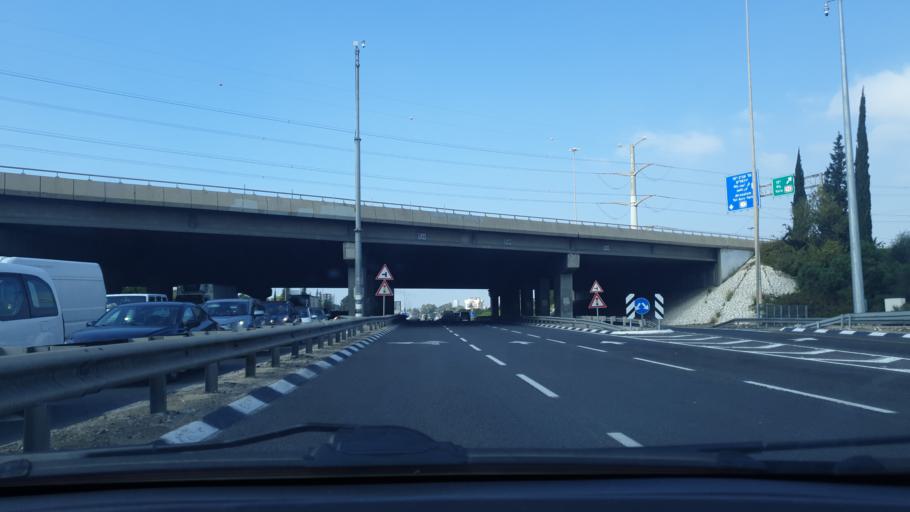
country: IL
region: Central District
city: Bet Dagan
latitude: 32.0097
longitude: 34.8148
